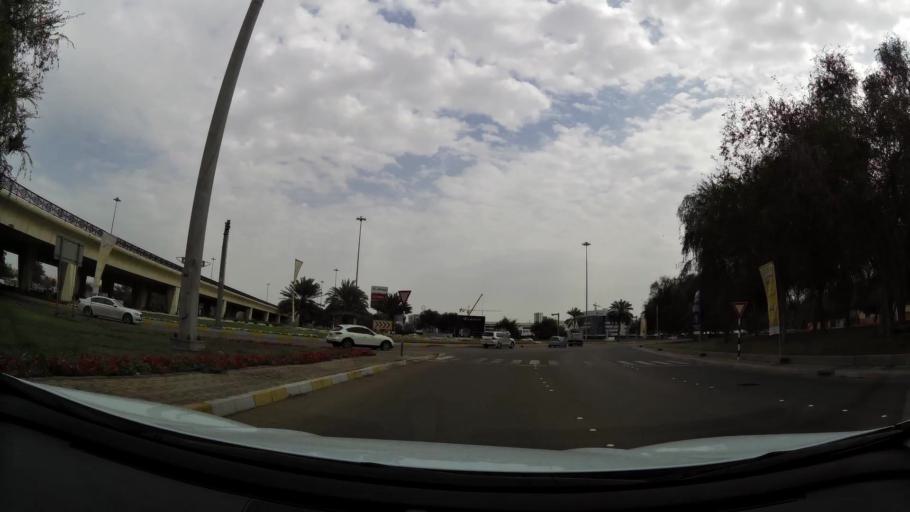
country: AE
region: Abu Dhabi
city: Abu Dhabi
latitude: 24.4259
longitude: 54.4440
